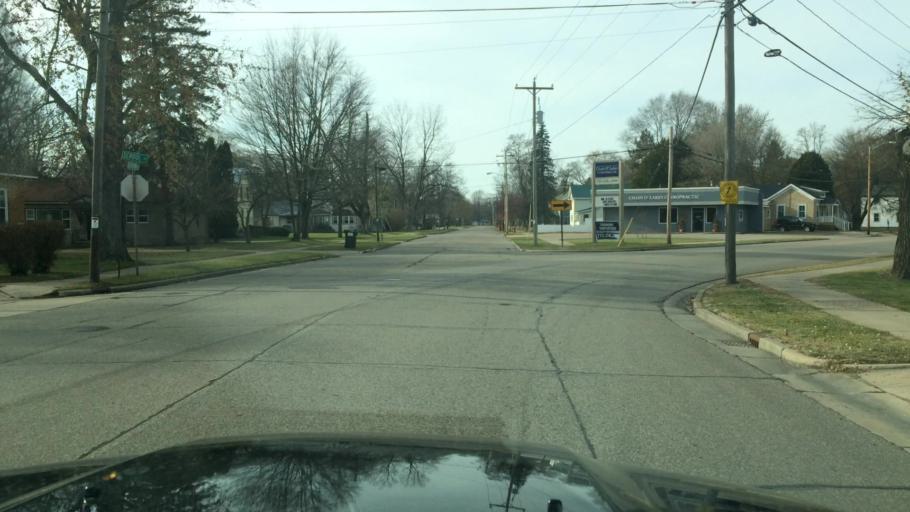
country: US
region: Wisconsin
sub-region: Waupaca County
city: Waupaca
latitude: 44.3515
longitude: -89.0738
